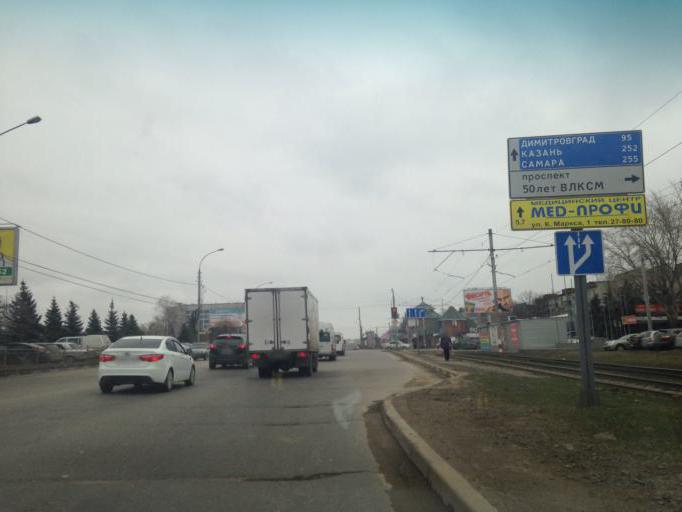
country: RU
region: Ulyanovsk
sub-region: Ulyanovskiy Rayon
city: Ulyanovsk
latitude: 54.3084
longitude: 48.3302
